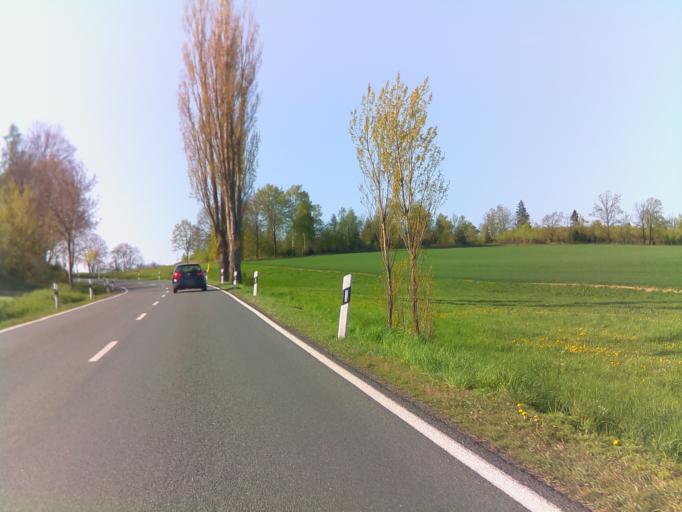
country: DE
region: Thuringia
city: Kospoda
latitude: 50.7098
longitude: 11.7666
